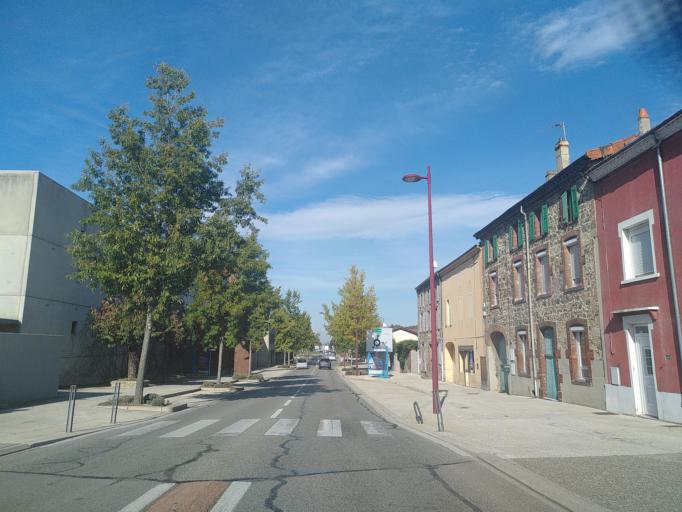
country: FR
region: Rhone-Alpes
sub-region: Departement de l'Ardeche
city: Sarras
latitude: 45.2017
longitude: 4.8149
